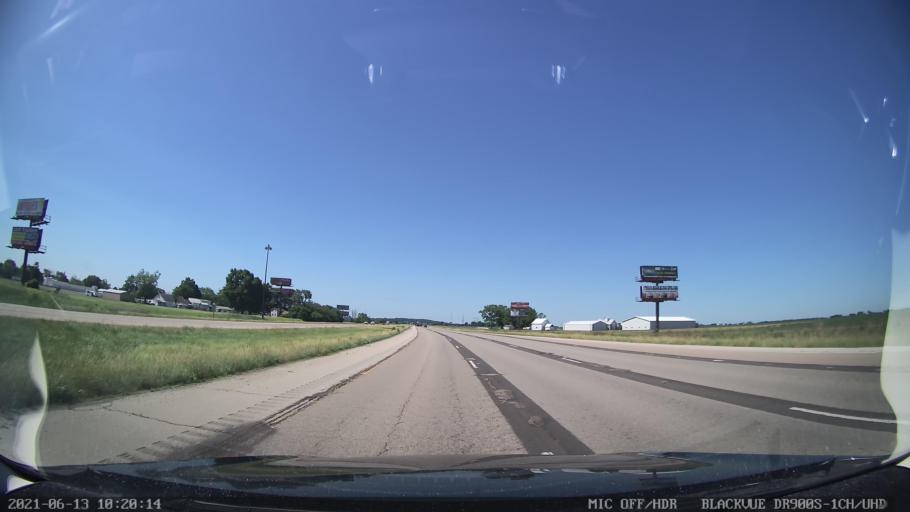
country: US
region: Illinois
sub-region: Logan County
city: Lincoln
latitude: 40.0724
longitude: -89.4451
